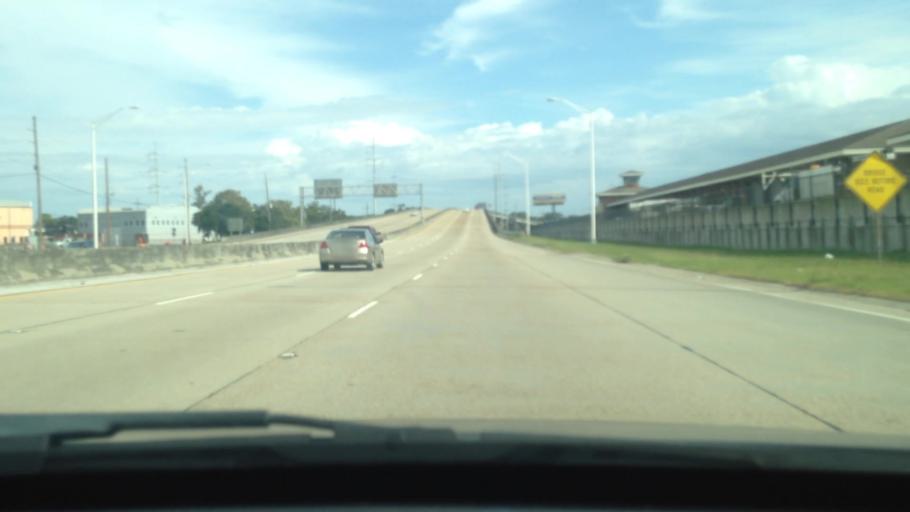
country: US
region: Louisiana
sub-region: Jefferson Parish
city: Metairie Terrace
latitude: 29.9692
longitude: -90.1770
